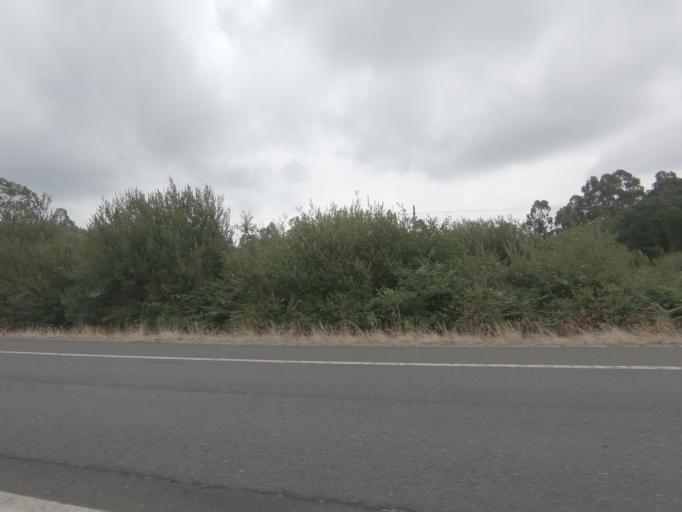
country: ES
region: Galicia
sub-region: Provincia de Pontevedra
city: Tomino
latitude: 41.9653
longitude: -8.7602
